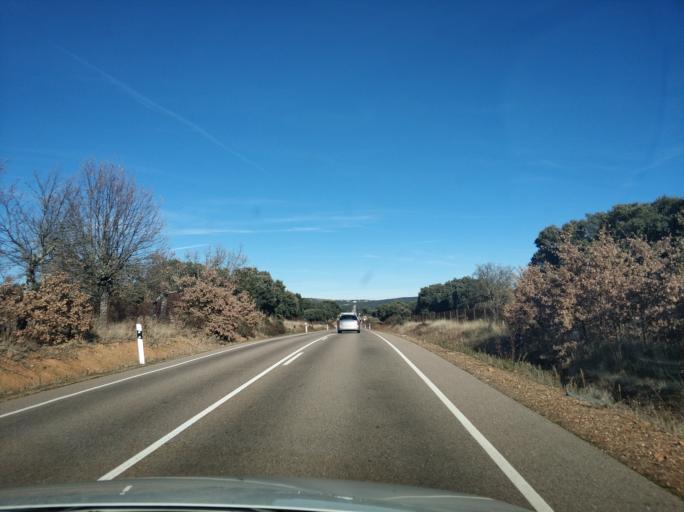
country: ES
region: Castille and Leon
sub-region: Provincia de Salamanca
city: Narros de Matalayegua
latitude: 40.6755
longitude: -5.8948
